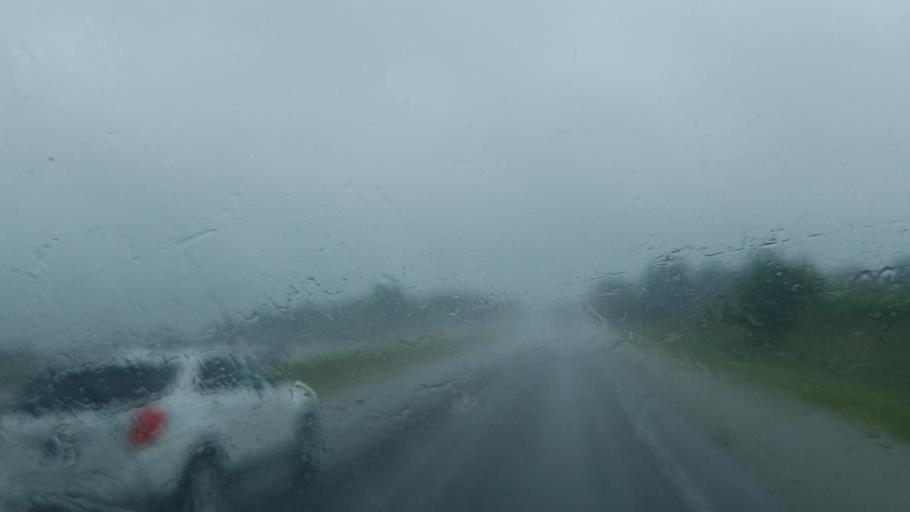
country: US
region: Indiana
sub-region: Delaware County
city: Yorktown
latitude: 40.2619
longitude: -85.5578
